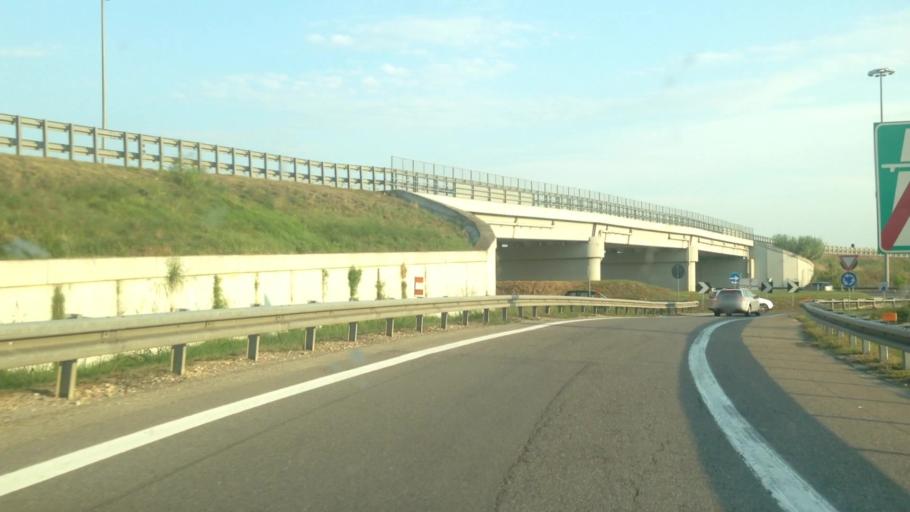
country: IT
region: Piedmont
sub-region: Provincia di Asti
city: Azzano d'Asti
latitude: 44.9073
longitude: 8.2542
